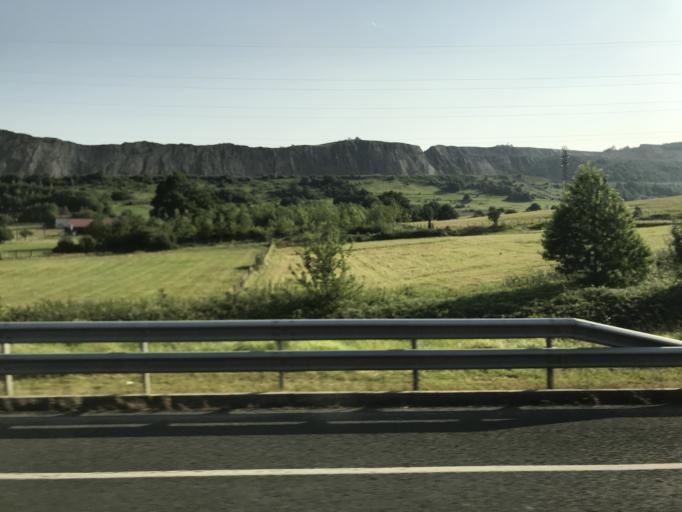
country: ES
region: Navarre
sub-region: Provincia de Navarra
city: Altsasu
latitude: 42.9186
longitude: -2.2018
